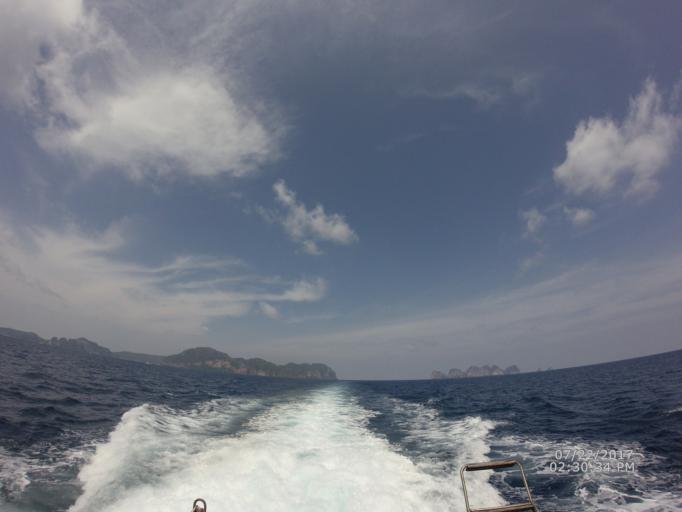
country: TH
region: Phangnga
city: Ban Phru Nai
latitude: 7.7379
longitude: 98.7180
